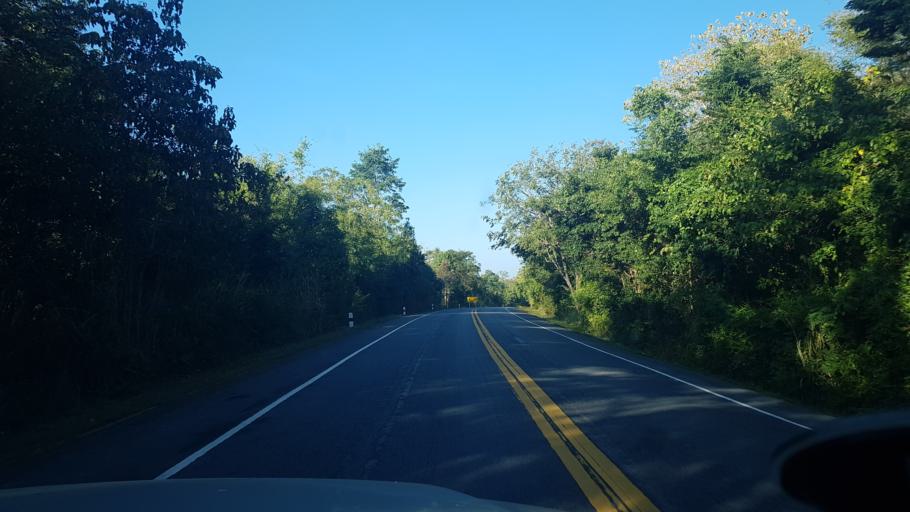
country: TH
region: Phetchabun
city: Nam Nao
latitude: 16.6960
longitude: 101.6363
